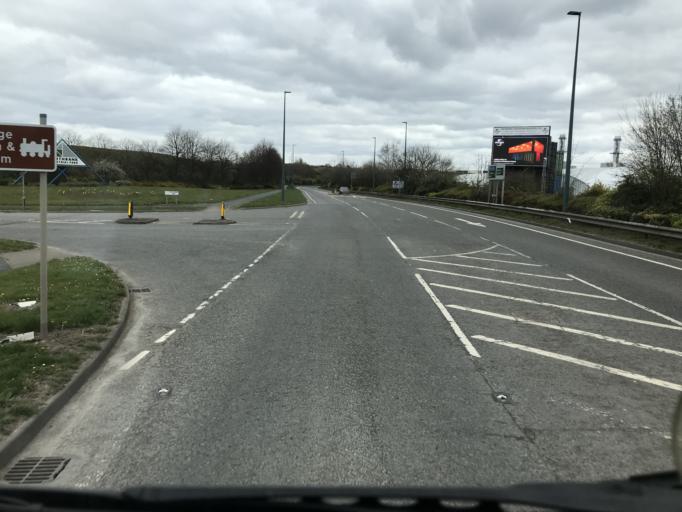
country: GB
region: England
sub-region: City and Borough of Salford
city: Irlam
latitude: 53.4331
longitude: -2.4214
